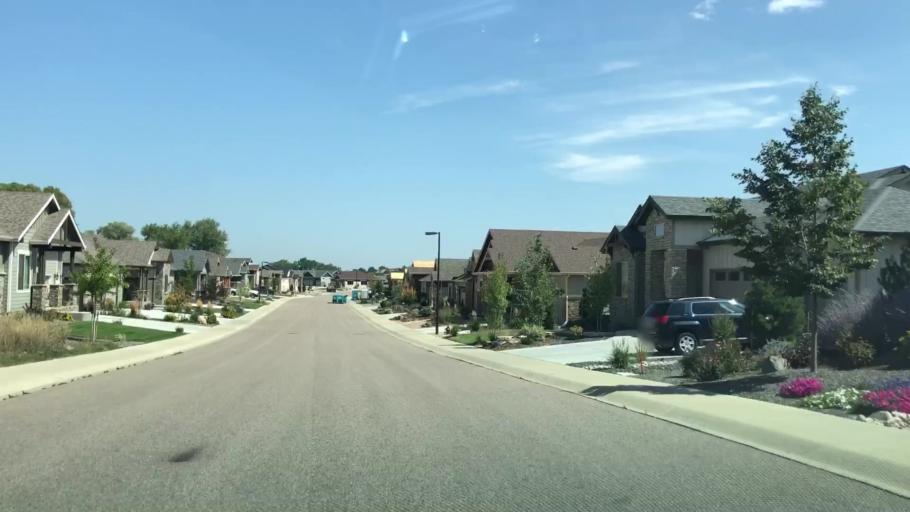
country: US
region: Colorado
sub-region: Larimer County
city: Loveland
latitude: 40.3974
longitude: -105.1569
